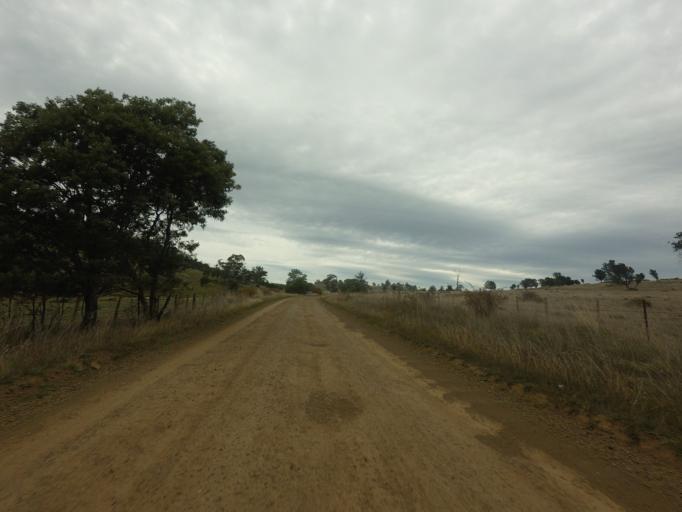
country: AU
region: Tasmania
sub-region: Derwent Valley
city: New Norfolk
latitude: -42.5581
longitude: 146.9186
